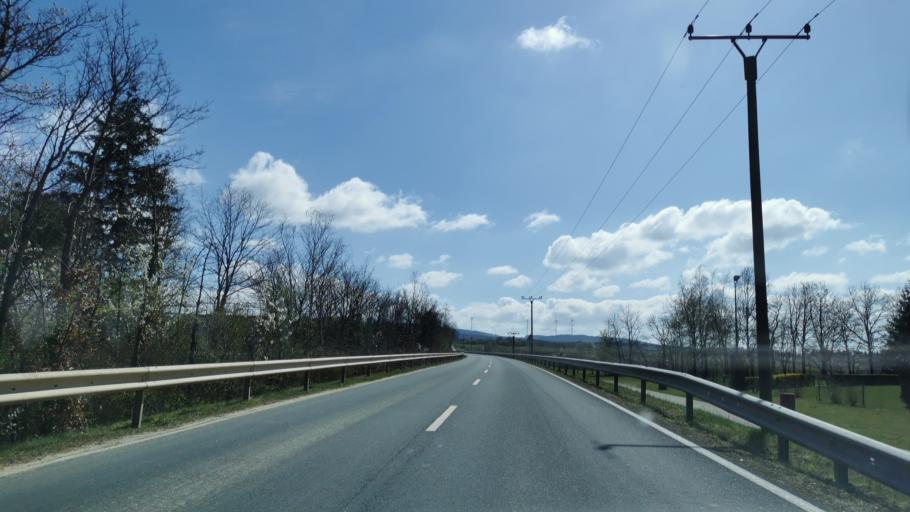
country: DE
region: Rheinland-Pfalz
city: Minheim
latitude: 49.8625
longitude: 6.9236
